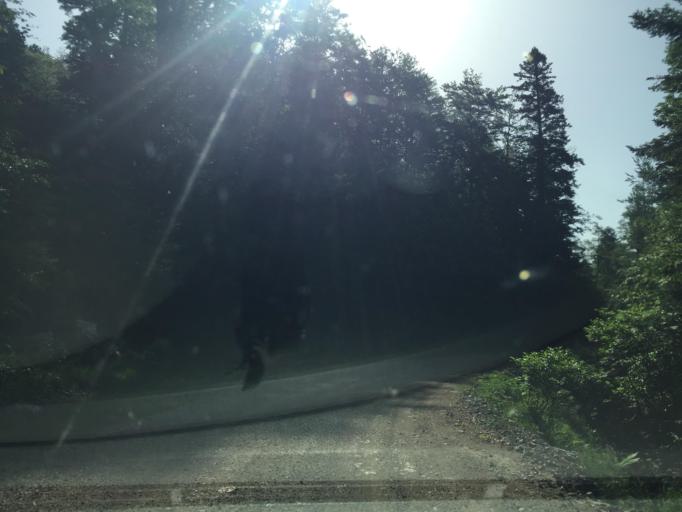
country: HR
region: Primorsko-Goranska
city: Podhum
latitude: 45.4743
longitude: 14.5212
